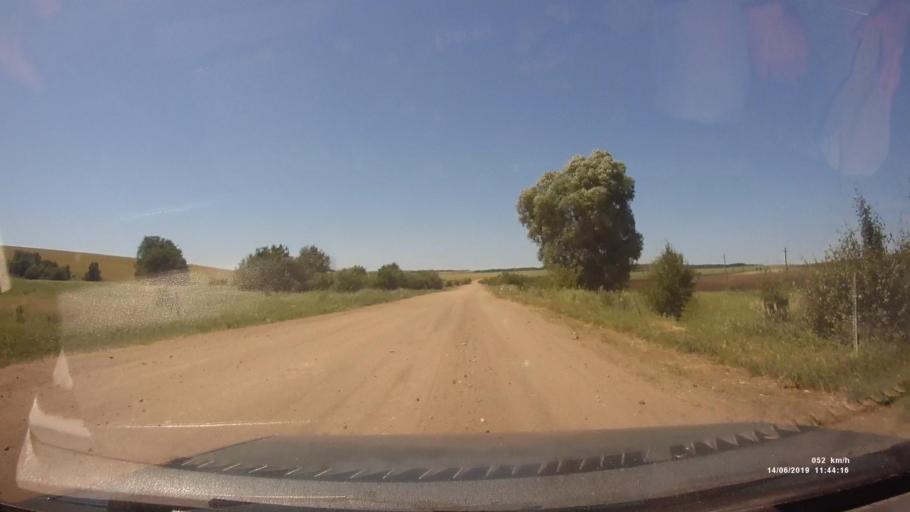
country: RU
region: Rostov
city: Kazanskaya
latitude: 49.8552
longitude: 41.3255
